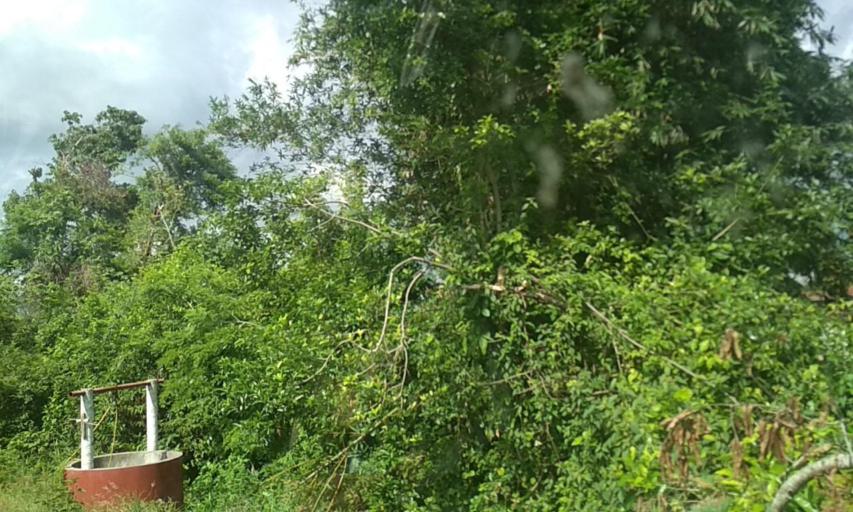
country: MX
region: Puebla
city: San Jose Acateno
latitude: 20.2832
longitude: -97.1302
